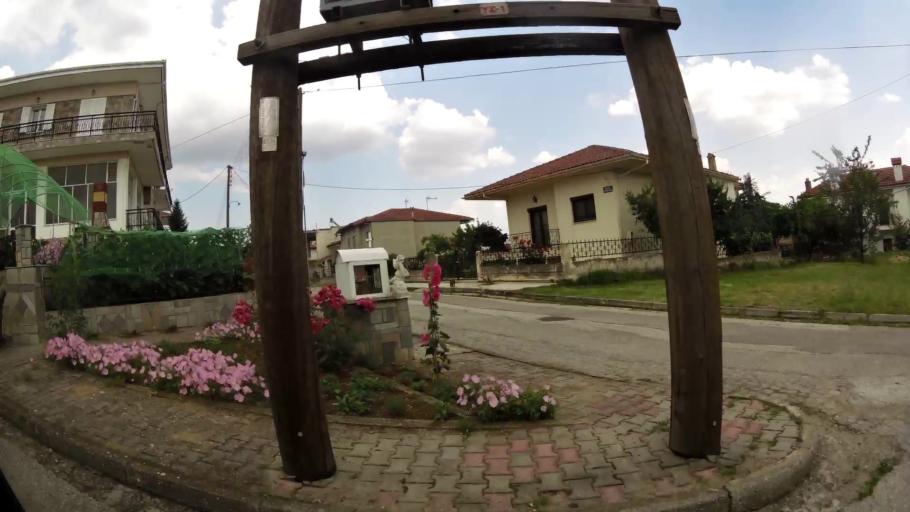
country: GR
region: West Macedonia
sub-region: Nomos Kozanis
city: Koila
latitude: 40.3218
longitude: 21.8209
